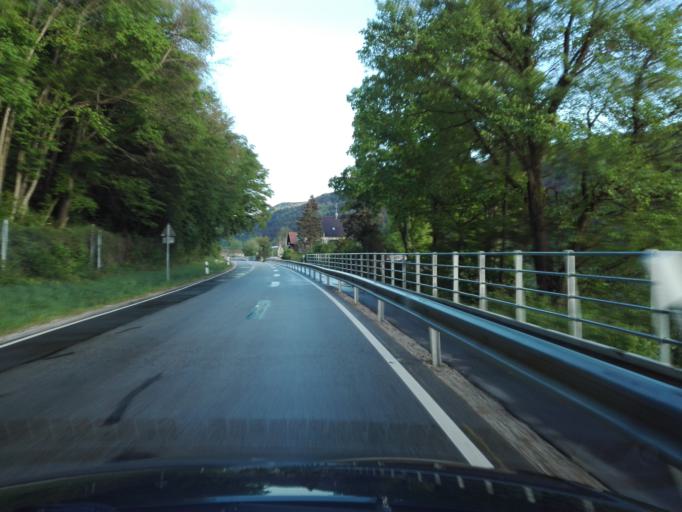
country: DE
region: Bavaria
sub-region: Lower Bavaria
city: Obernzell
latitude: 48.5398
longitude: 13.6610
